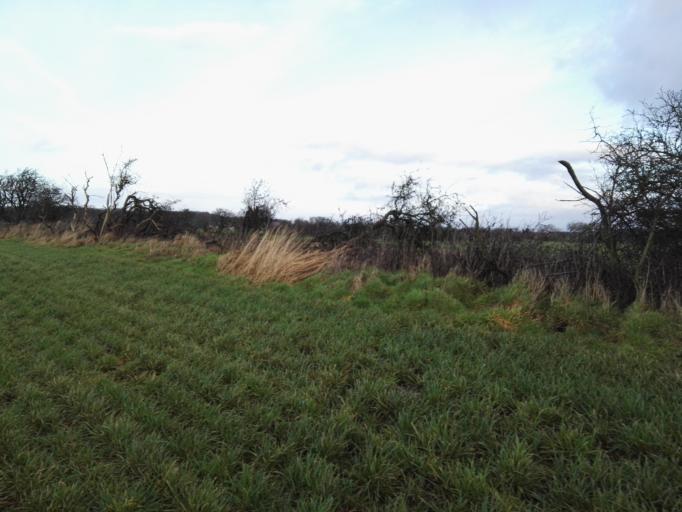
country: DK
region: Capital Region
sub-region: Frederikssund Kommune
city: Jaegerspris
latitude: 55.8467
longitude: 11.9735
